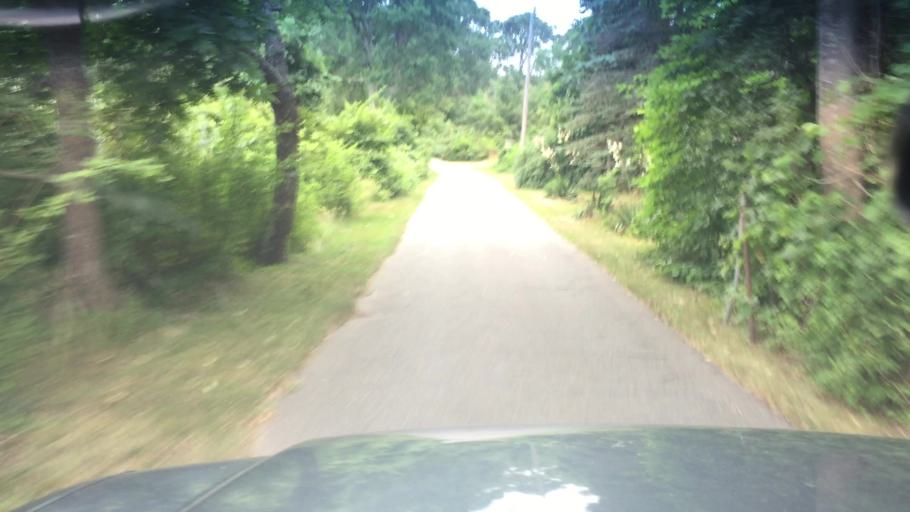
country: US
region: Massachusetts
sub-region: Barnstable County
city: Pocasset
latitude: 41.6936
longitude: -70.6176
